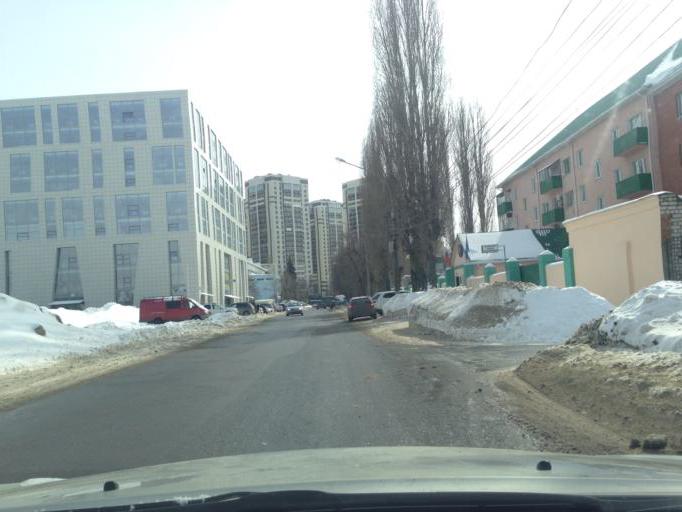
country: RU
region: Voronezj
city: Voronezh
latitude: 51.6579
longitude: 39.1760
